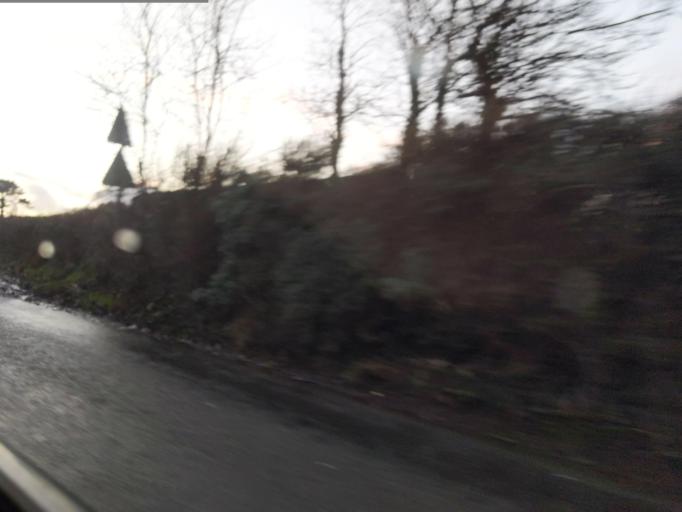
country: GB
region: England
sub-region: Devon
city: Fremington
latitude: 51.0580
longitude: -4.0860
